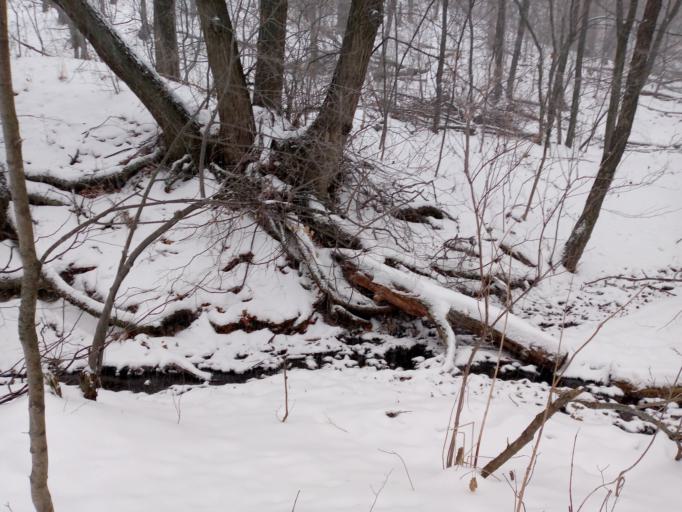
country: RU
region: Saratov
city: Krasnyy Oktyabr'
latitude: 51.3435
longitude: 45.7807
